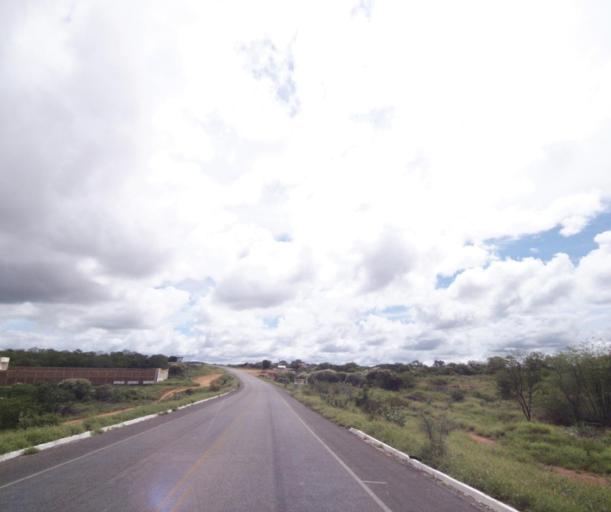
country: BR
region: Bahia
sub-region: Brumado
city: Brumado
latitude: -14.2316
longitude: -41.6809
